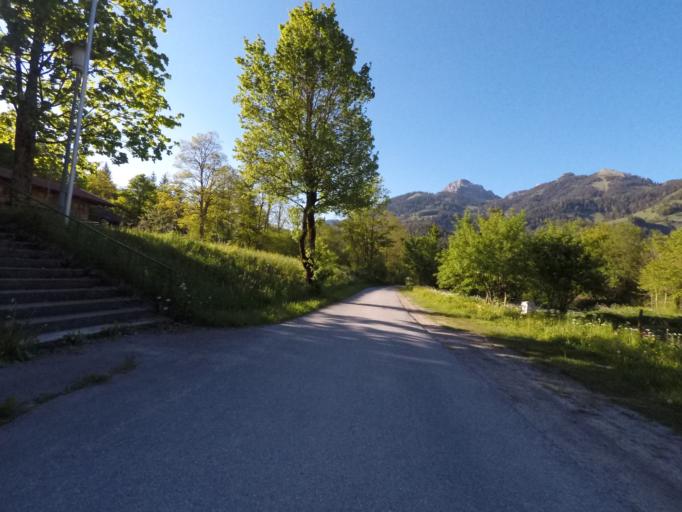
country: DE
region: Bavaria
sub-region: Upper Bavaria
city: Bayrischzell
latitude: 47.6706
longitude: 12.0107
